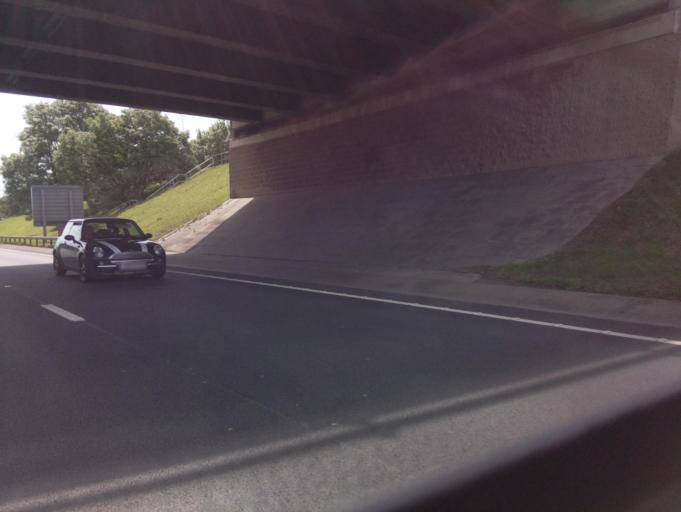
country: GB
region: England
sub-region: Redcar and Cleveland
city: Thornaby-on-Tees
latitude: 54.5483
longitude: -1.2752
